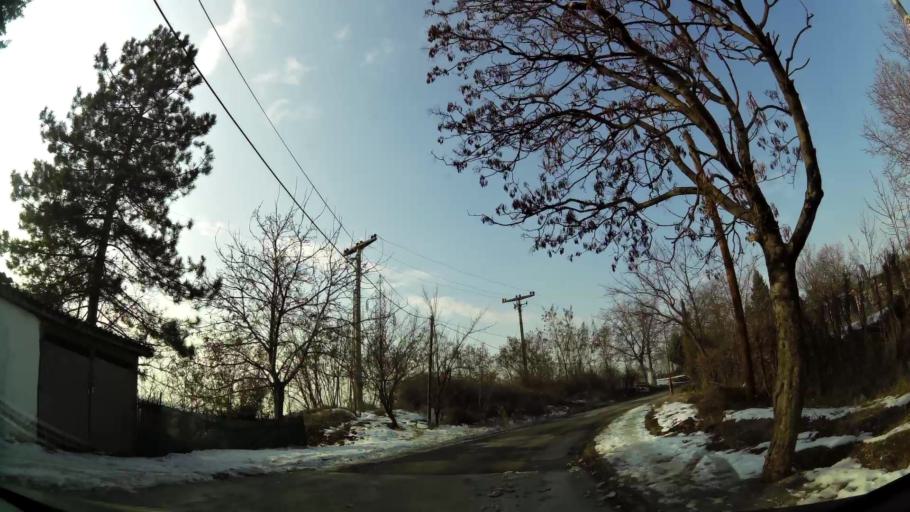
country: MK
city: Creshevo
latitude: 42.0120
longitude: 21.5008
